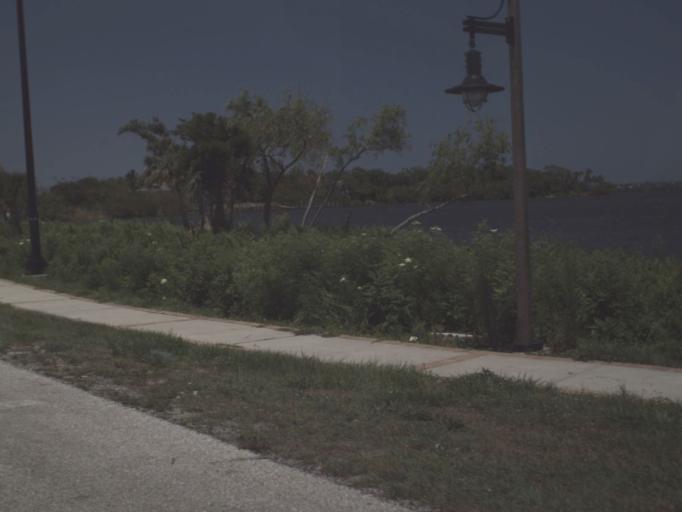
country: US
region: Florida
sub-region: Brevard County
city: Palm Bay
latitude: 28.0357
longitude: -80.5819
